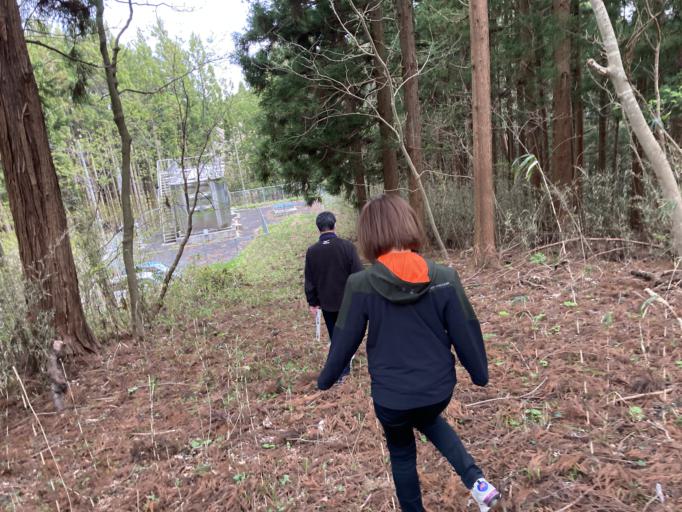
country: JP
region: Iwate
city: Ichinoseki
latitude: 38.9675
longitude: 141.1912
